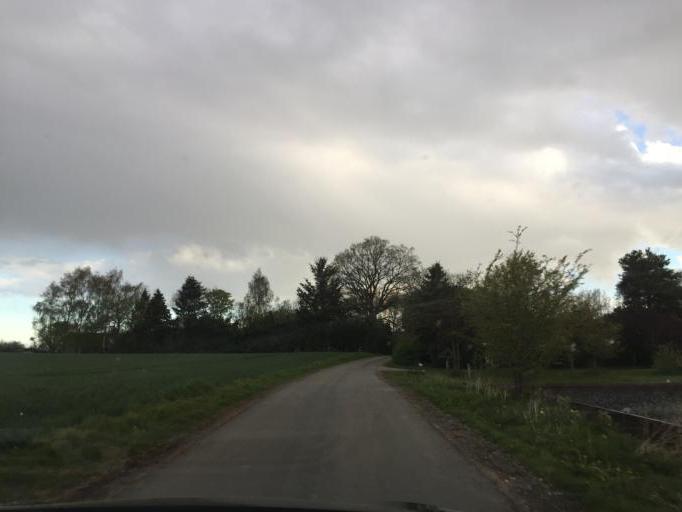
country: DK
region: Zealand
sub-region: Koge Kommune
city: Borup
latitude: 55.5194
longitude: 11.9905
